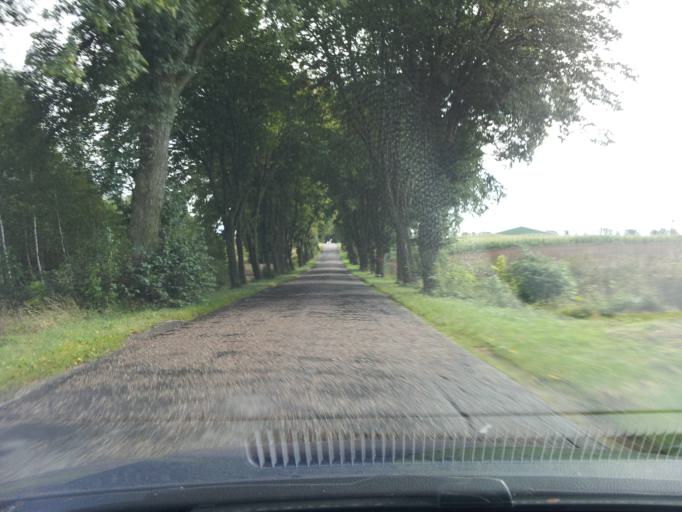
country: PL
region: Kujawsko-Pomorskie
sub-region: Powiat brodnicki
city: Gorzno
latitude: 53.2151
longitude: 19.6350
